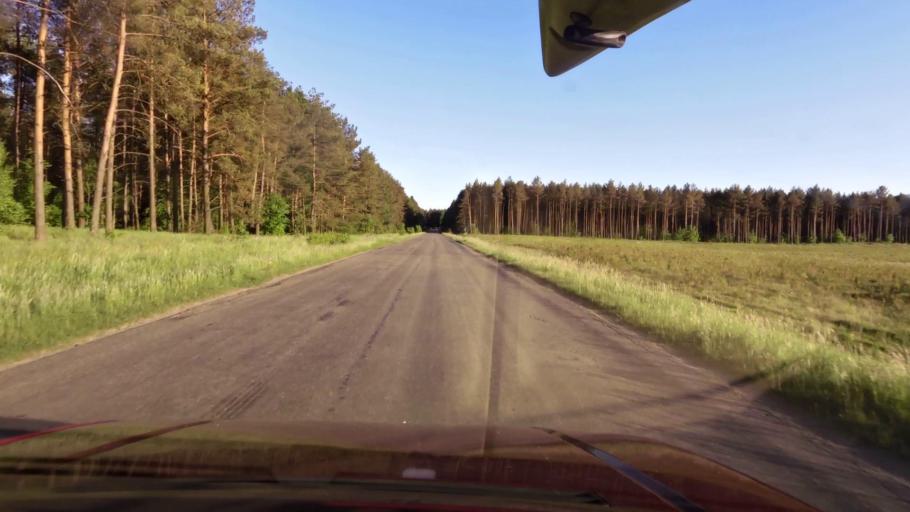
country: PL
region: West Pomeranian Voivodeship
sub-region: Powiat szczecinecki
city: Bialy Bor
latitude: 53.9036
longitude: 16.8129
